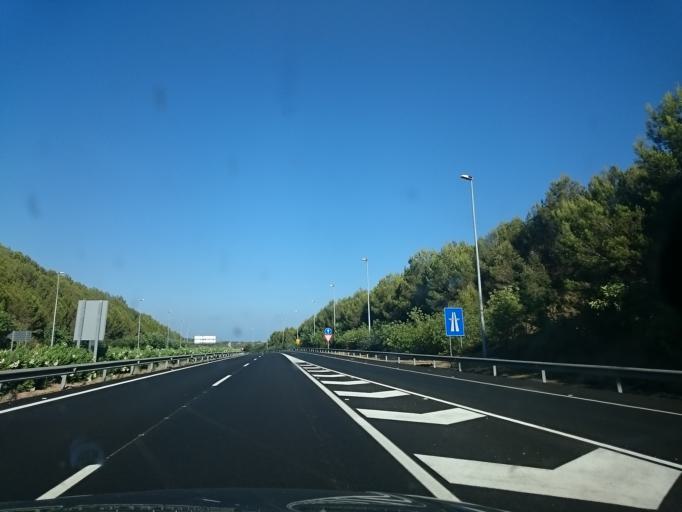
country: ES
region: Catalonia
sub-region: Provincia de Tarragona
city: Cunit
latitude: 41.2124
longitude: 1.6167
